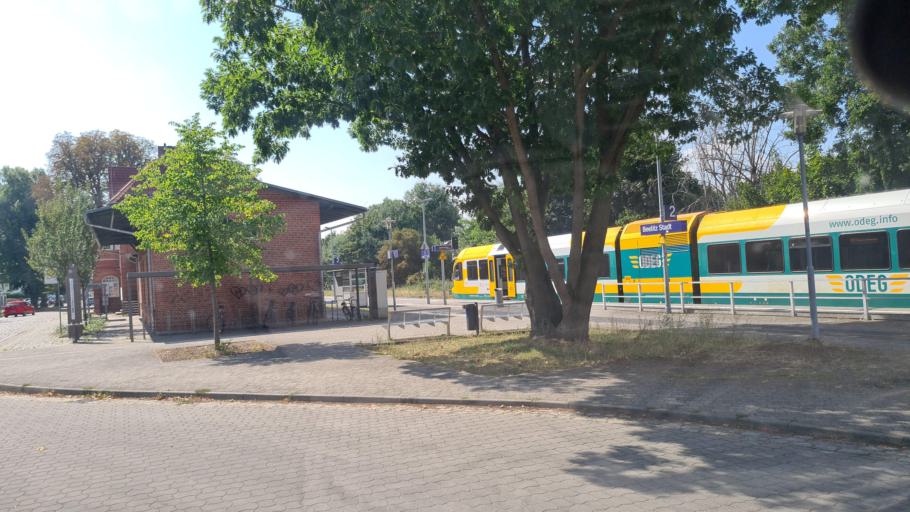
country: DE
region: Brandenburg
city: Beelitz
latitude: 52.2397
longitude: 12.9671
